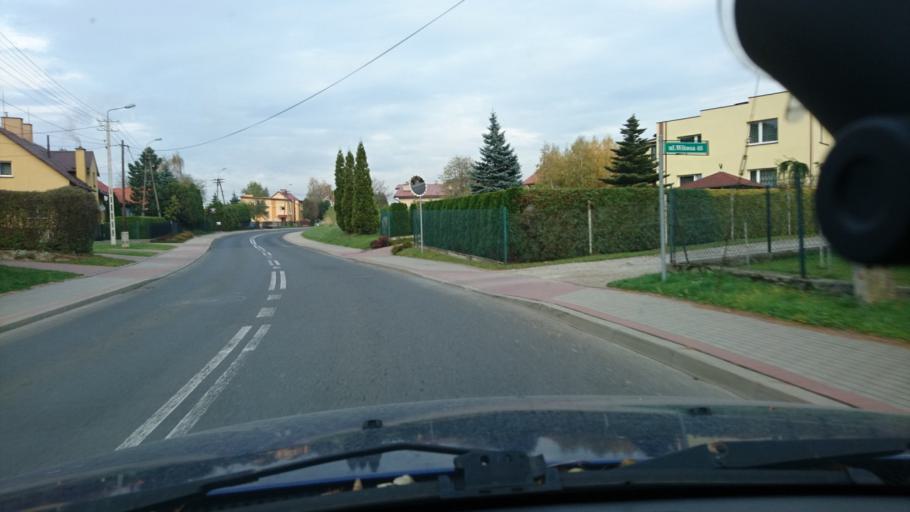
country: PL
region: Silesian Voivodeship
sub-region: Bielsko-Biala
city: Bielsko-Biala
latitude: 49.8408
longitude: 19.0858
